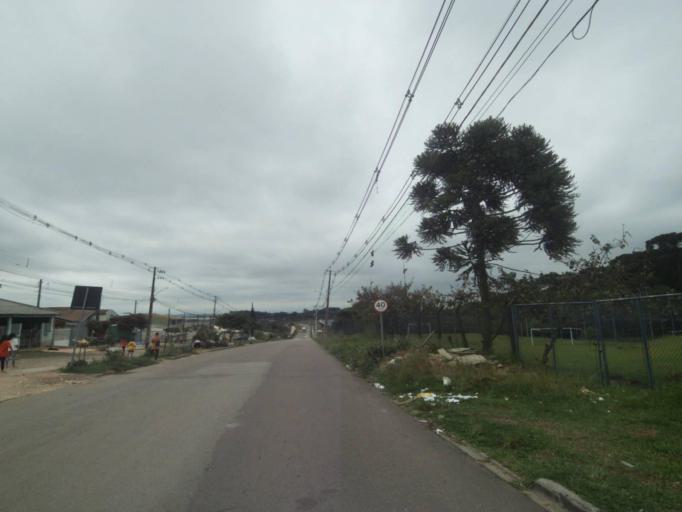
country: BR
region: Parana
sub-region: Araucaria
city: Araucaria
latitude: -25.5590
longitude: -49.3129
